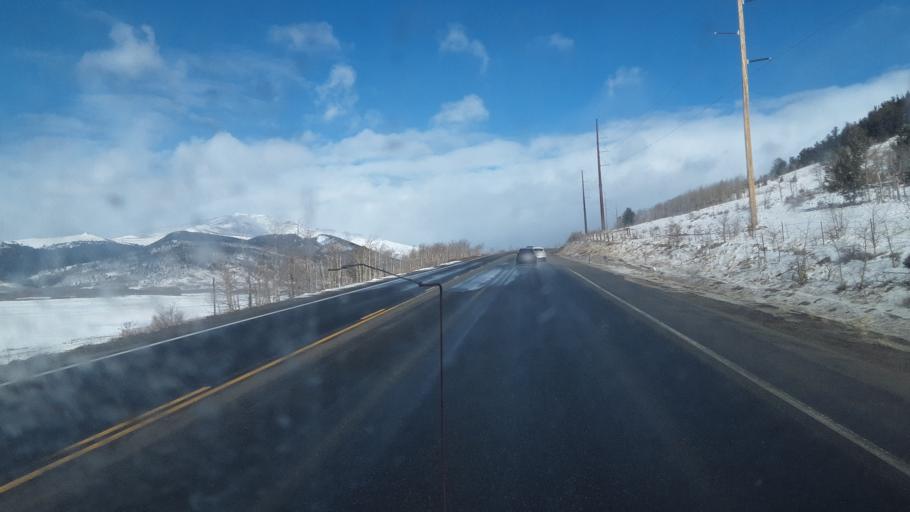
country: US
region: Colorado
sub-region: Park County
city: Fairplay
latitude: 39.2533
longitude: -105.9633
